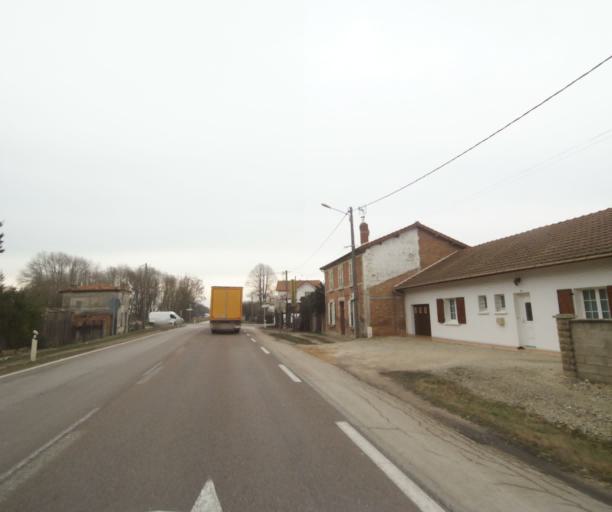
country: FR
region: Champagne-Ardenne
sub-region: Departement de la Haute-Marne
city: Villiers-en-Lieu
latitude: 48.6465
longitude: 4.8725
